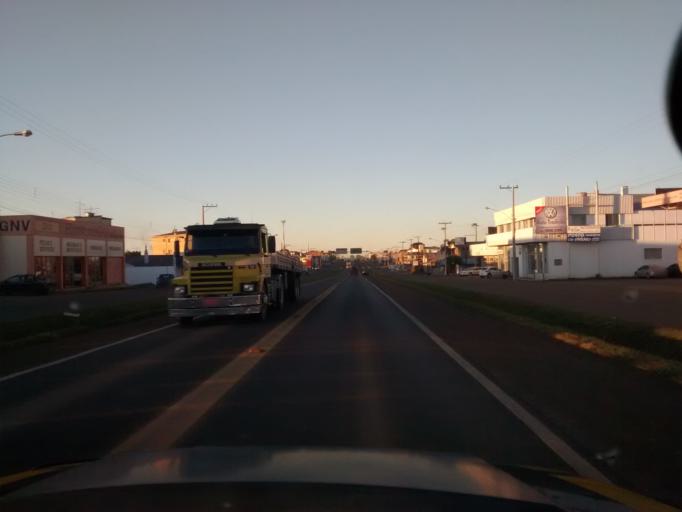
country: BR
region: Rio Grande do Sul
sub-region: Vacaria
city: Vacaria
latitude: -28.5198
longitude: -50.9410
